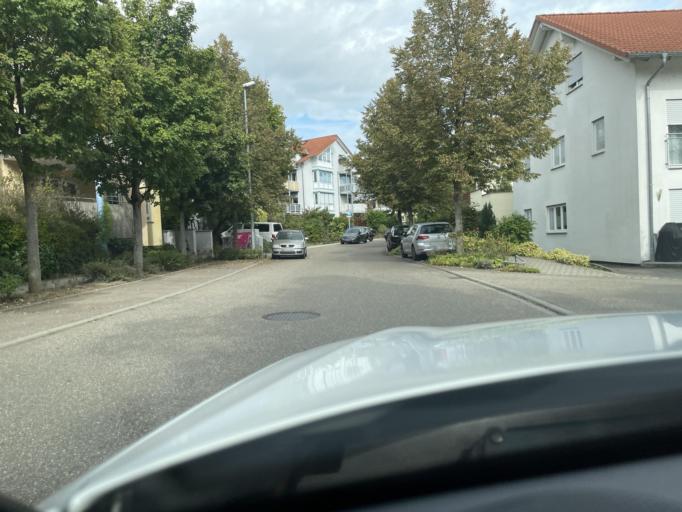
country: DE
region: Baden-Wuerttemberg
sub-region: Regierungsbezirk Stuttgart
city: Marbach am Neckar
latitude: 48.9314
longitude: 9.2603
